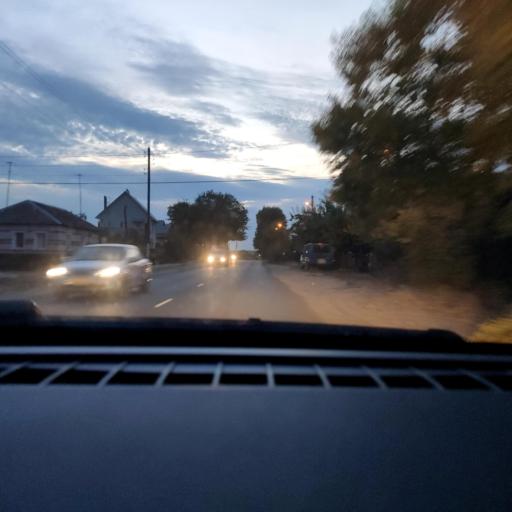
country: RU
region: Voronezj
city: Somovo
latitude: 51.7348
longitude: 39.2749
